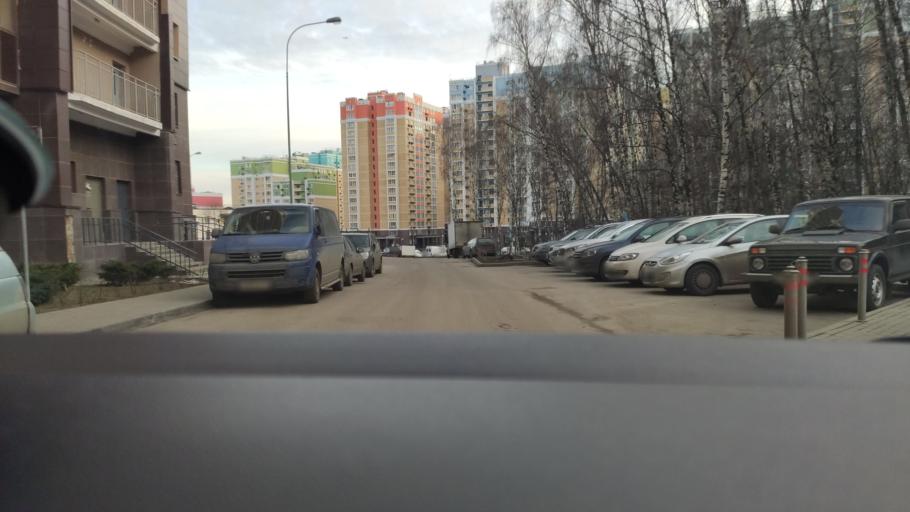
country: RU
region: Moskovskaya
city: Vidnoye
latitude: 55.5361
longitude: 37.7220
